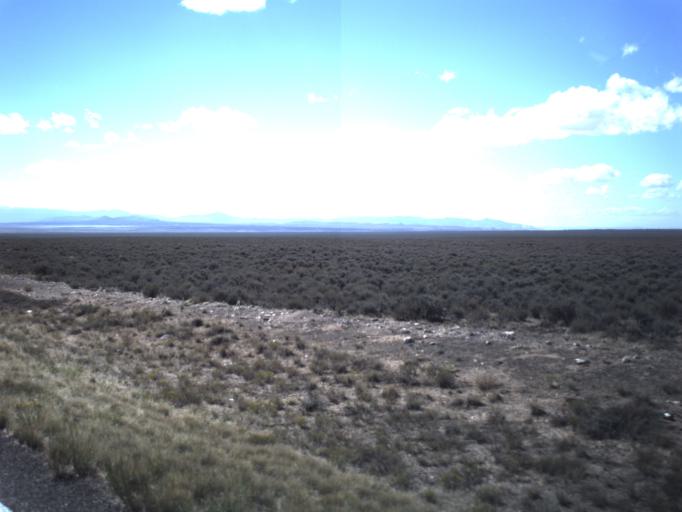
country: US
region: Utah
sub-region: Iron County
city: Enoch
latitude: 37.9741
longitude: -113.0052
